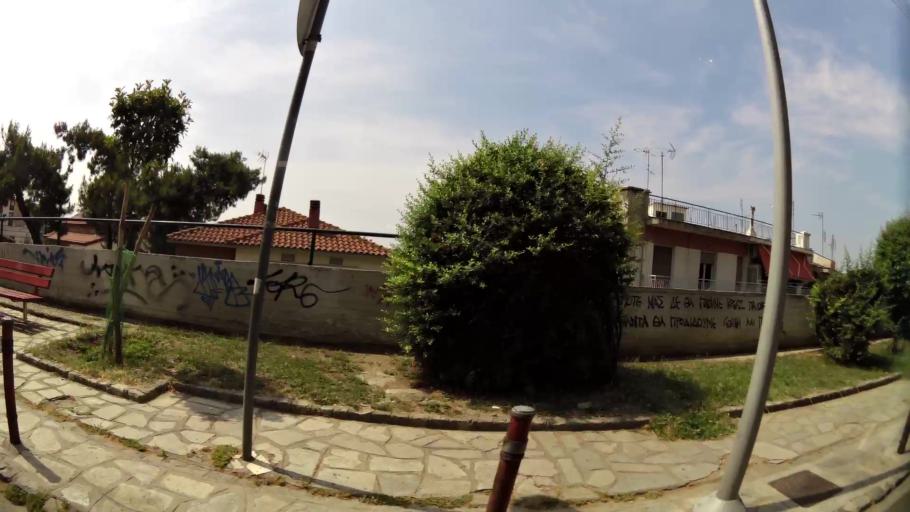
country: GR
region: Central Macedonia
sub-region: Nomos Thessalonikis
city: Agios Pavlos
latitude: 40.6401
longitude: 22.9543
